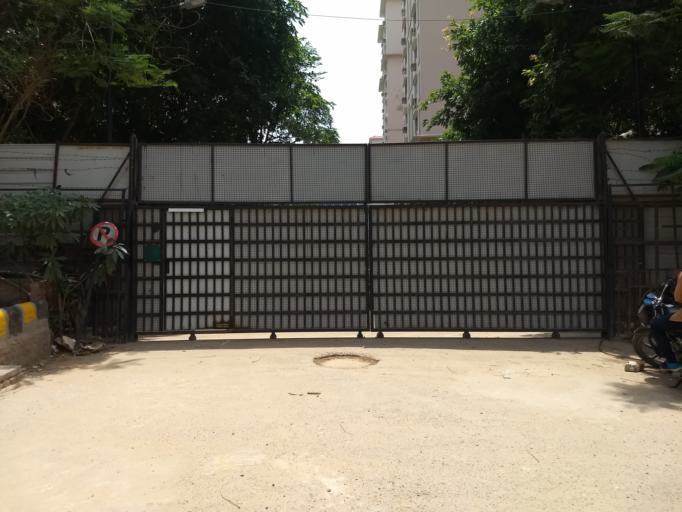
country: IN
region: Haryana
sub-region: Gurgaon
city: Gurgaon
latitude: 28.4493
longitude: 77.0987
